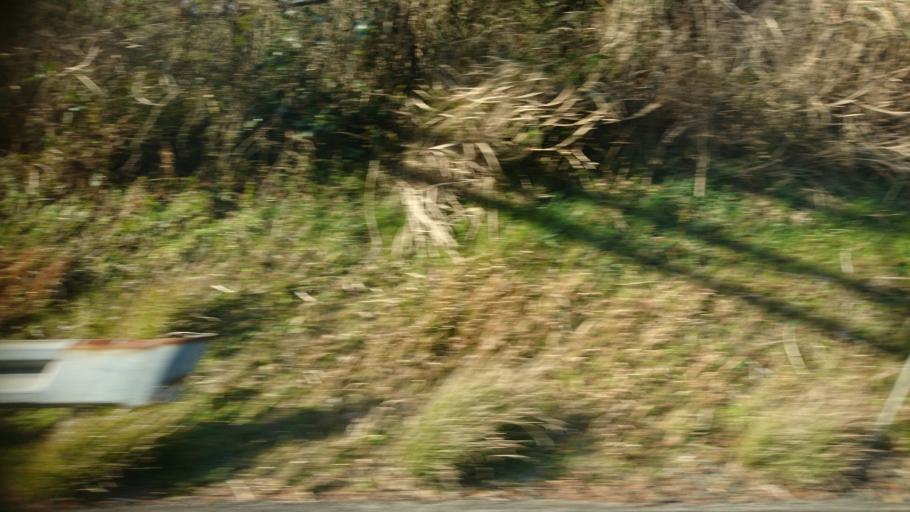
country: JP
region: Miyazaki
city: Kobayashi
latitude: 32.0371
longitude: 130.8164
